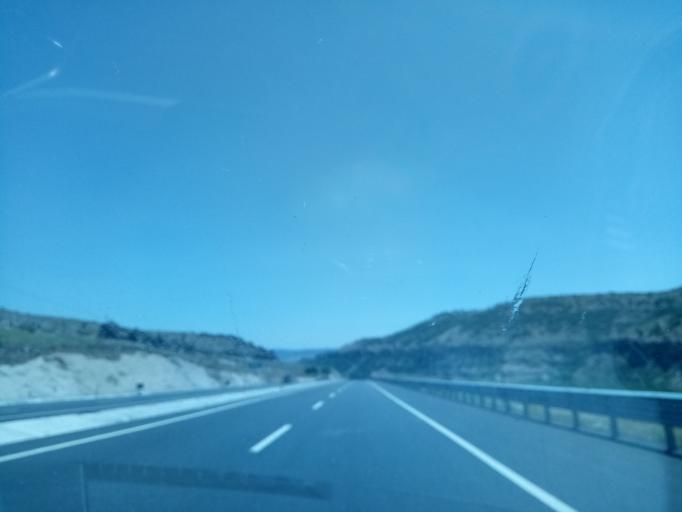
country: TR
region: Konya
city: Kiziloren
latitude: 37.7452
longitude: 32.1435
